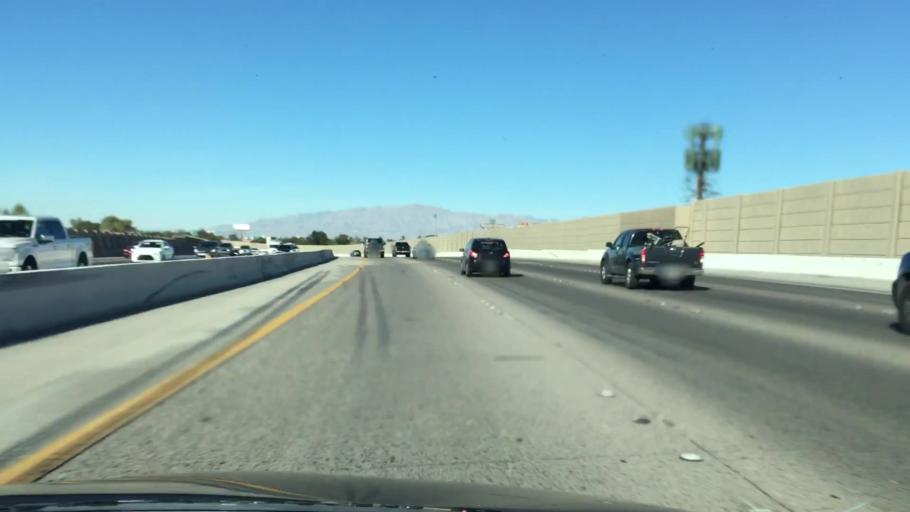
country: US
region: Nevada
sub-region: Clark County
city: Winchester
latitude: 36.1217
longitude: -115.0831
